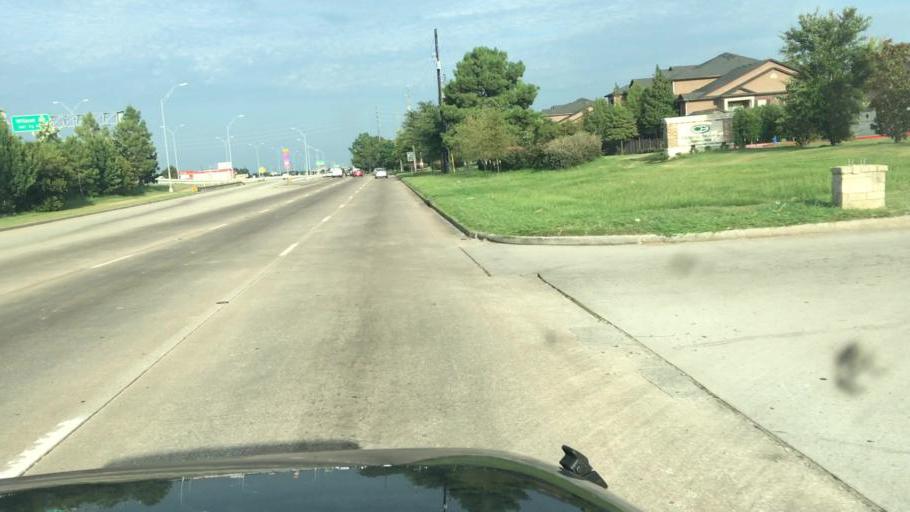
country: US
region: Texas
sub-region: Harris County
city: Humble
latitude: 29.9375
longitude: -95.2668
